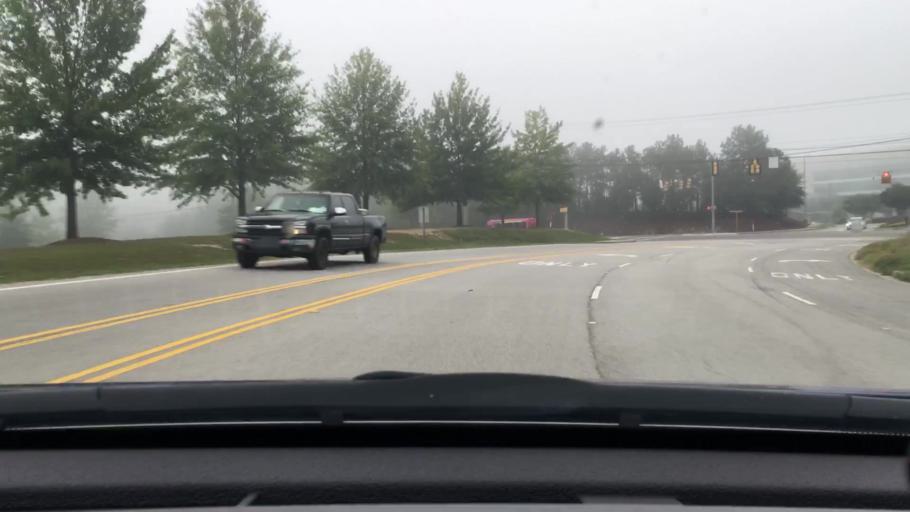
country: US
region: South Carolina
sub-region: Lexington County
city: Irmo
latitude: 34.0908
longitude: -81.1604
